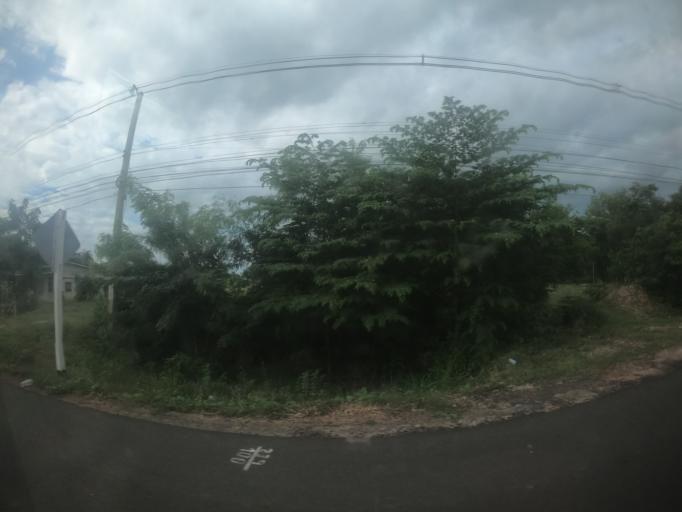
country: TH
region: Surin
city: Kap Choeng
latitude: 14.5486
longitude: 103.5118
